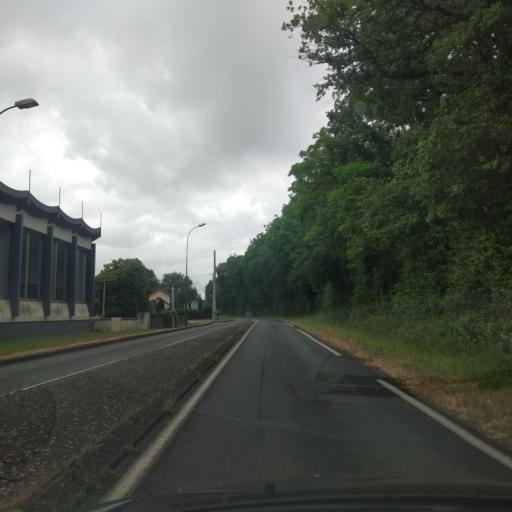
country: FR
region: Poitou-Charentes
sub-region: Departement de la Vienne
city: Vouneuil-sous-Biard
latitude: 46.5858
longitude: 0.2773
